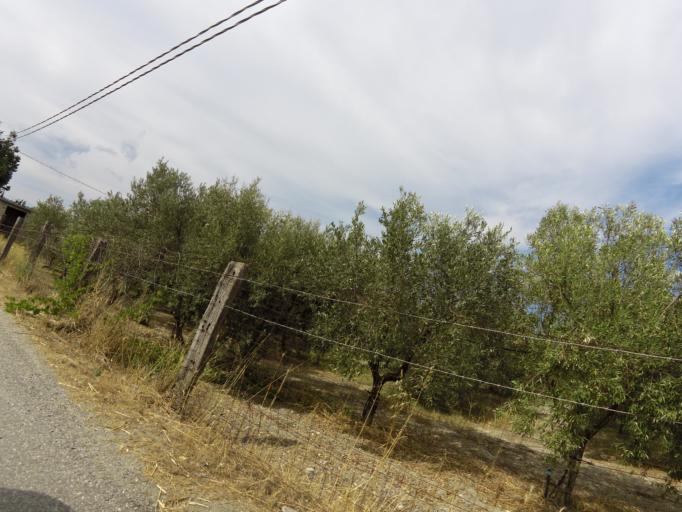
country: IT
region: Calabria
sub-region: Provincia di Reggio Calabria
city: Monasterace
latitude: 38.4534
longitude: 16.5176
